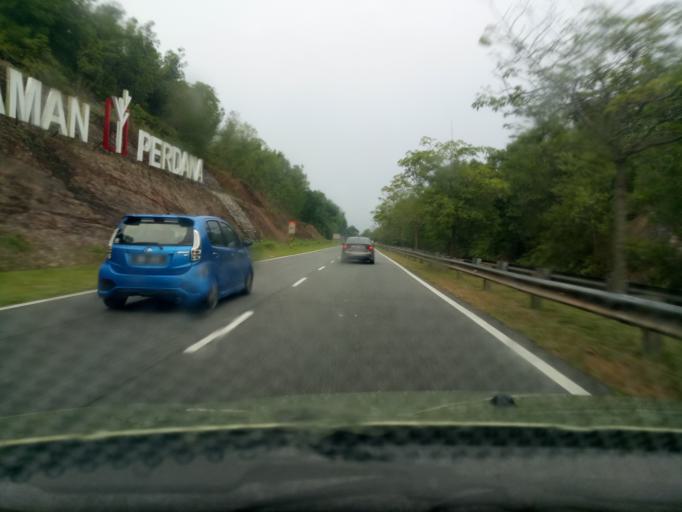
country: MY
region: Kedah
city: Sungai Petani
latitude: 5.6526
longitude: 100.5382
